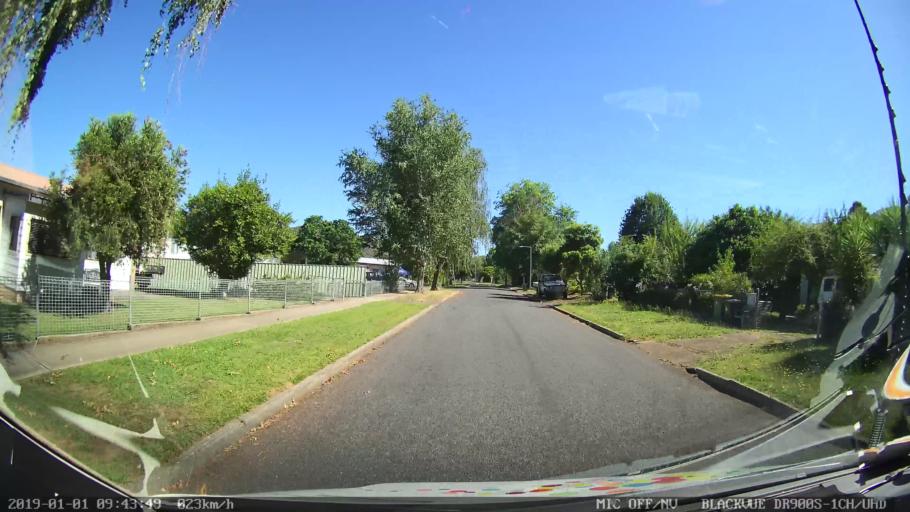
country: AU
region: New South Wales
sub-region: Snowy River
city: Jindabyne
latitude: -36.2139
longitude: 148.1351
